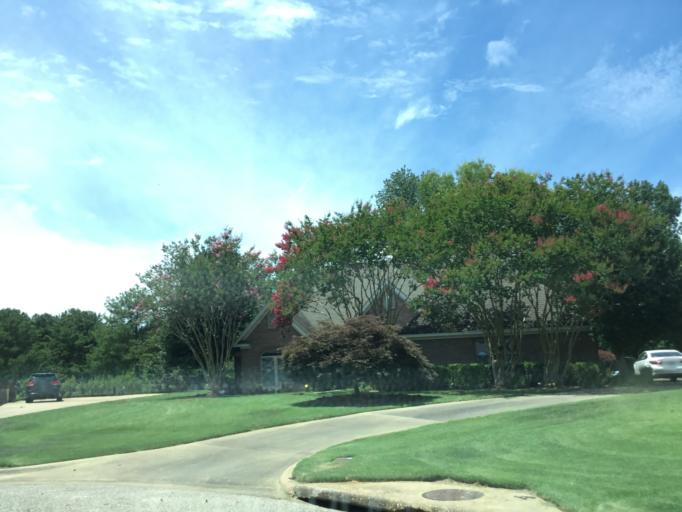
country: US
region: Alabama
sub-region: Montgomery County
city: Pike Road
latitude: 32.3776
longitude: -86.1365
